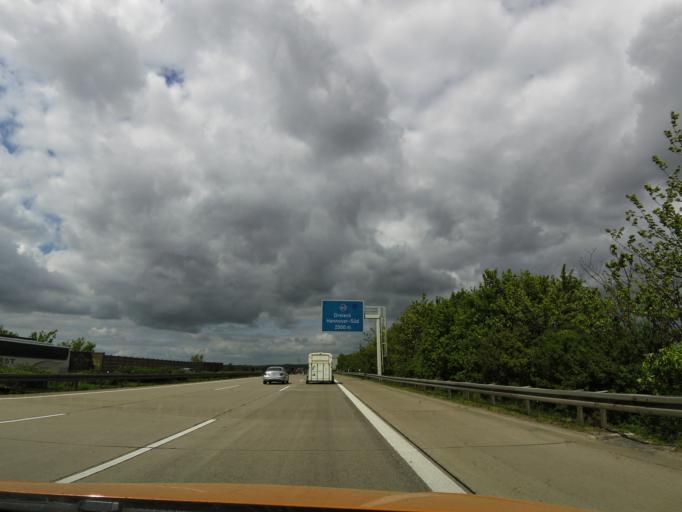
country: DE
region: Lower Saxony
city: Sehnde
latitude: 52.2832
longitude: 9.9062
